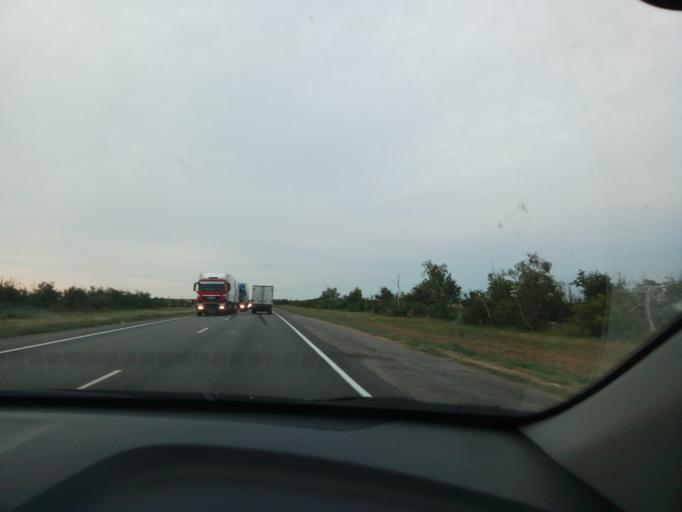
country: RU
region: Volgograd
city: Primorsk
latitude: 49.2123
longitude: 44.9037
